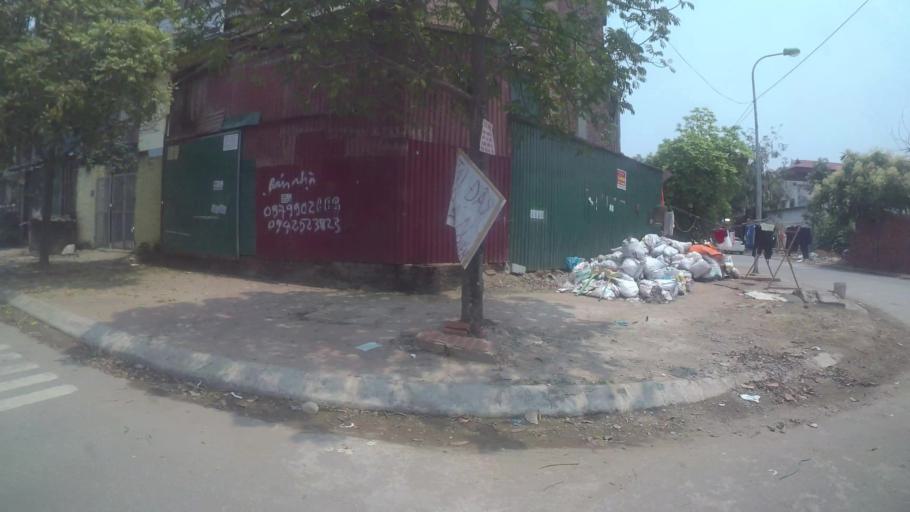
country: VN
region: Ha Noi
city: Ha Dong
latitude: 20.9924
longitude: 105.7779
